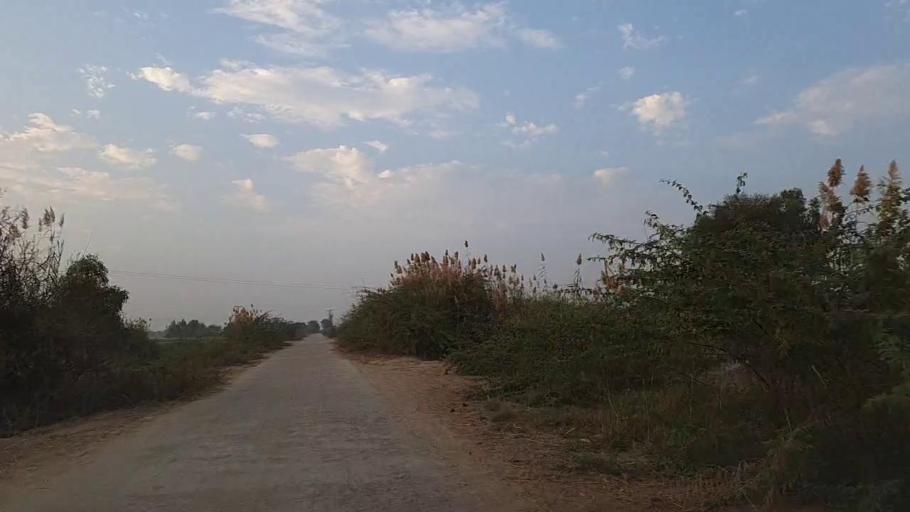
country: PK
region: Sindh
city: Mirwah Gorchani
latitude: 25.3377
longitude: 69.2090
